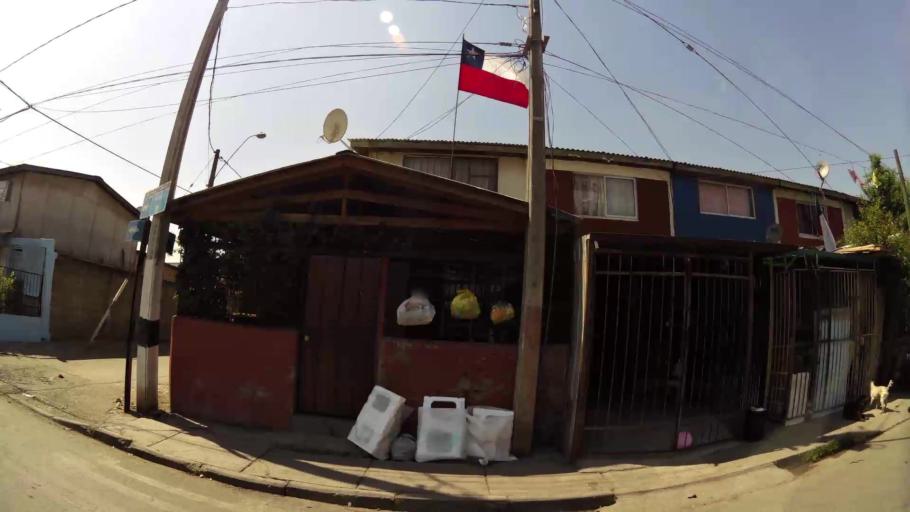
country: CL
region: Santiago Metropolitan
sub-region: Provincia de Santiago
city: La Pintana
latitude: -33.5573
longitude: -70.6139
